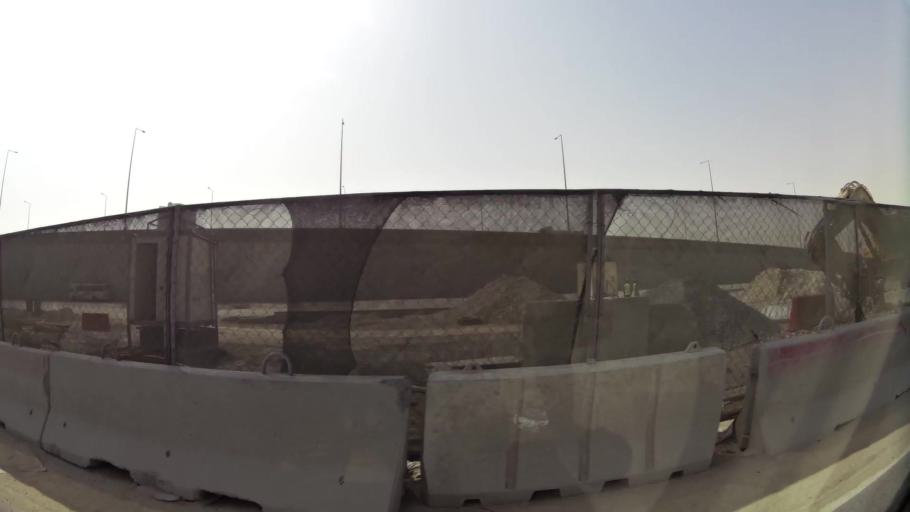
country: QA
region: Al Wakrah
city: Al Wukayr
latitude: 25.1922
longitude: 51.4529
